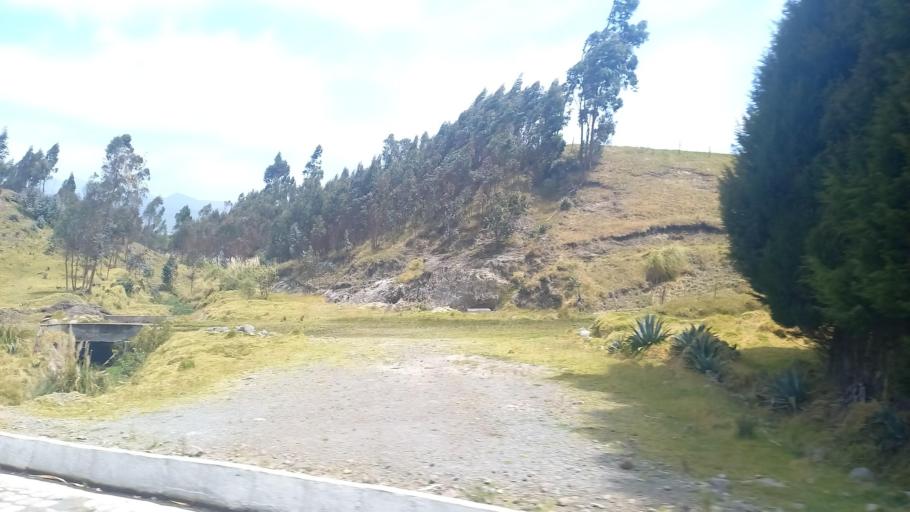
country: EC
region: Pichincha
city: Cayambe
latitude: 0.1609
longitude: -78.0786
